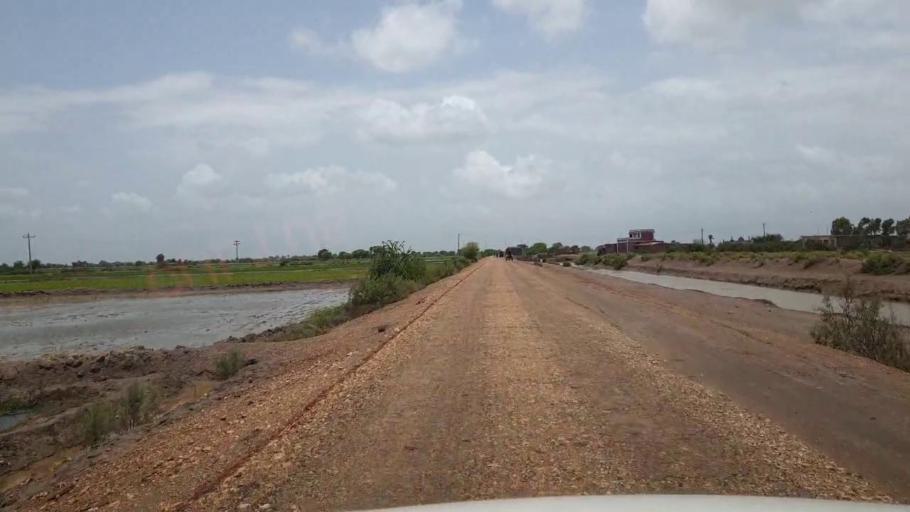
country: PK
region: Sindh
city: Kario
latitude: 24.7152
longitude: 68.5860
